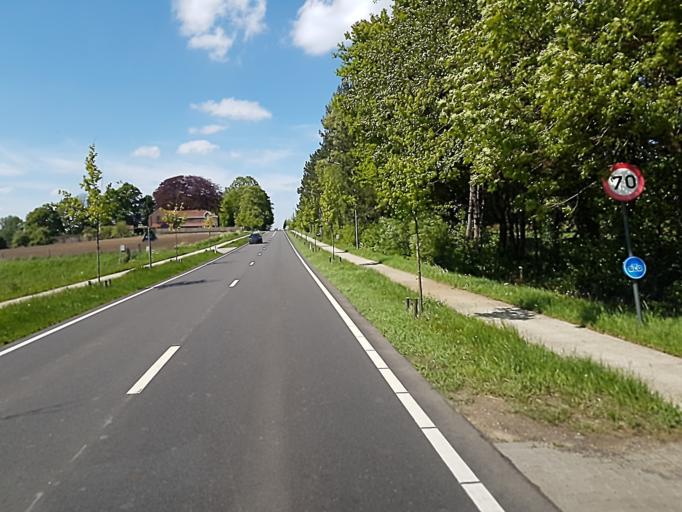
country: BE
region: Flanders
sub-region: Provincie Vlaams-Brabant
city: Glabbeek-Zuurbemde
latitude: 50.8494
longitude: 4.9061
